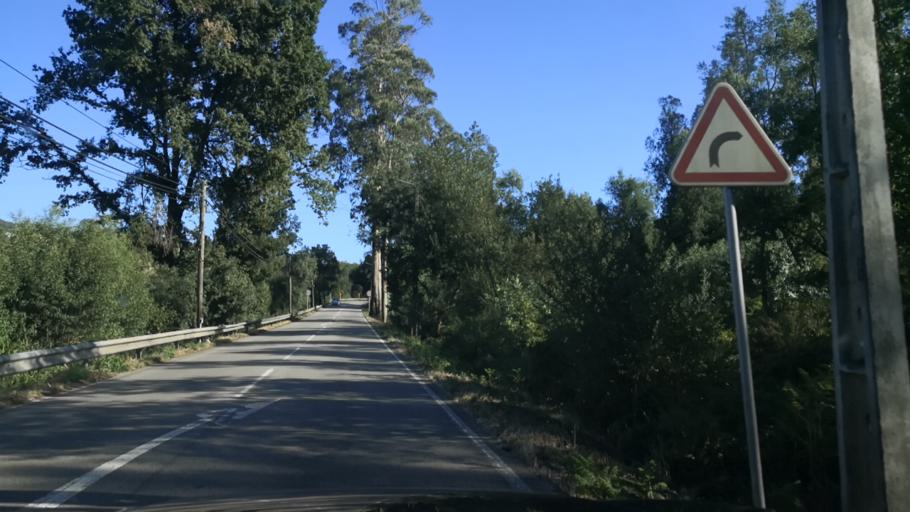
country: PT
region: Porto
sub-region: Pacos de Ferreira
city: Seroa
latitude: 41.2766
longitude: -8.4691
